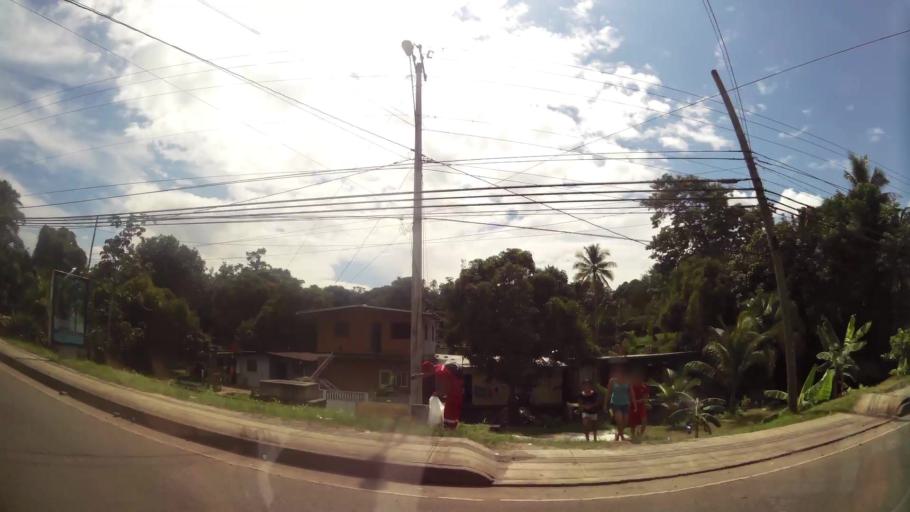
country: PA
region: Panama
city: Vista Alegre
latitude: 8.9333
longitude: -79.6932
